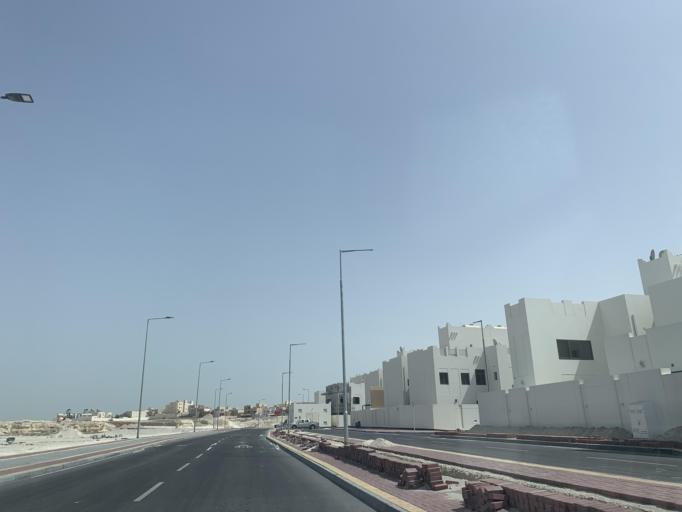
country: BH
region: Northern
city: Ar Rifa'
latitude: 26.1505
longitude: 50.5646
